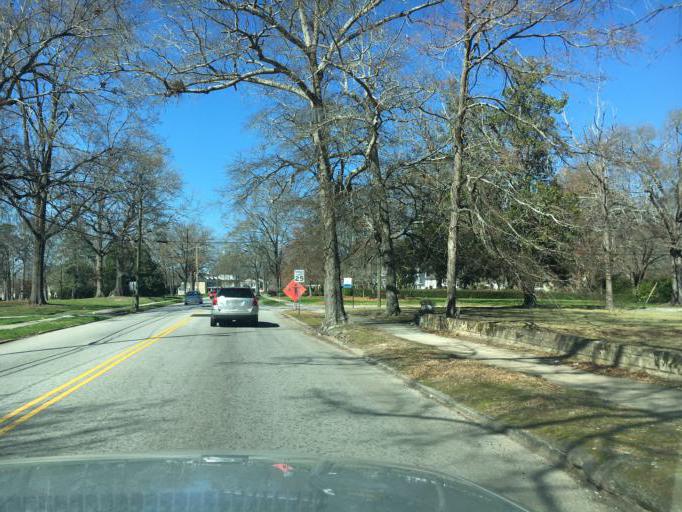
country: US
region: South Carolina
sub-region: Laurens County
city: Clinton
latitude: 34.4665
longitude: -81.8813
